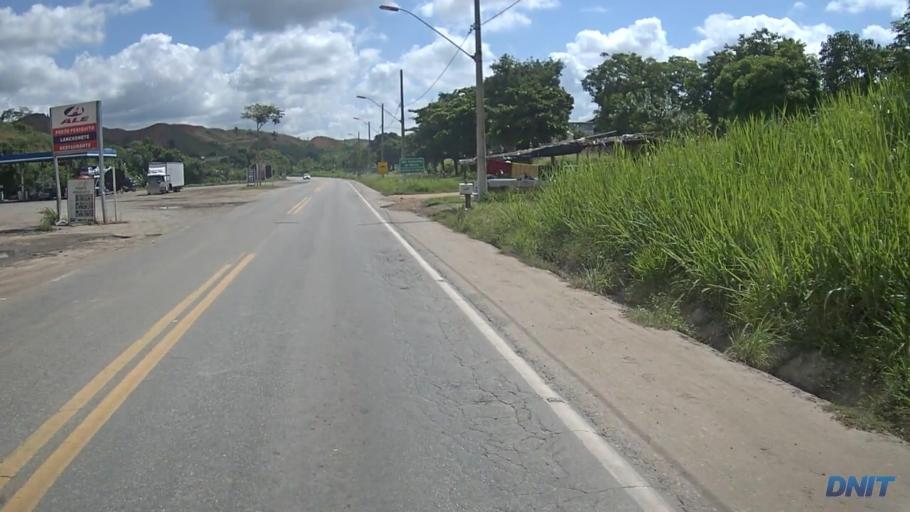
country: BR
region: Minas Gerais
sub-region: Belo Oriente
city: Belo Oriente
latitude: -19.1531
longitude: -42.2349
